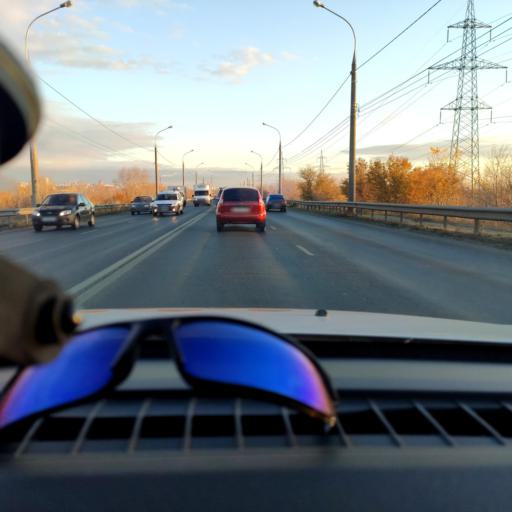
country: RU
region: Samara
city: Samara
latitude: 53.1574
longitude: 50.1915
